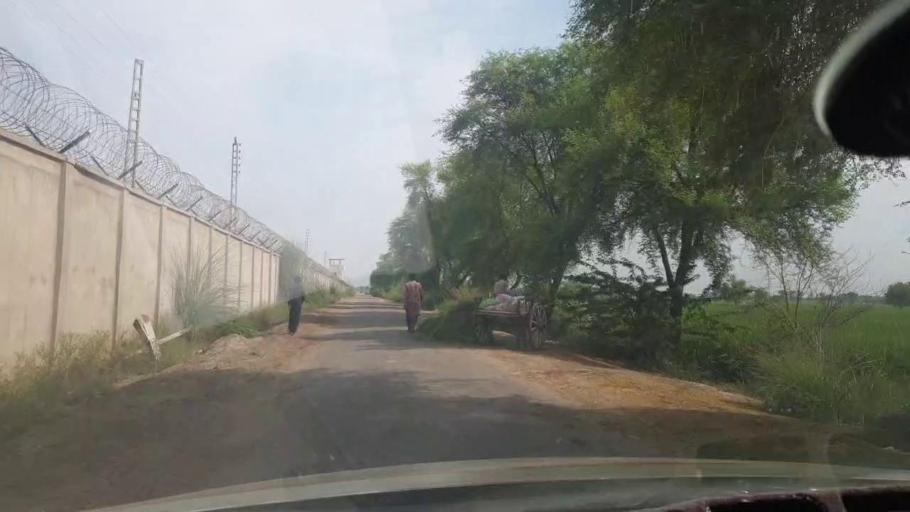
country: PK
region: Sindh
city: Jacobabad
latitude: 28.2752
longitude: 68.4805
